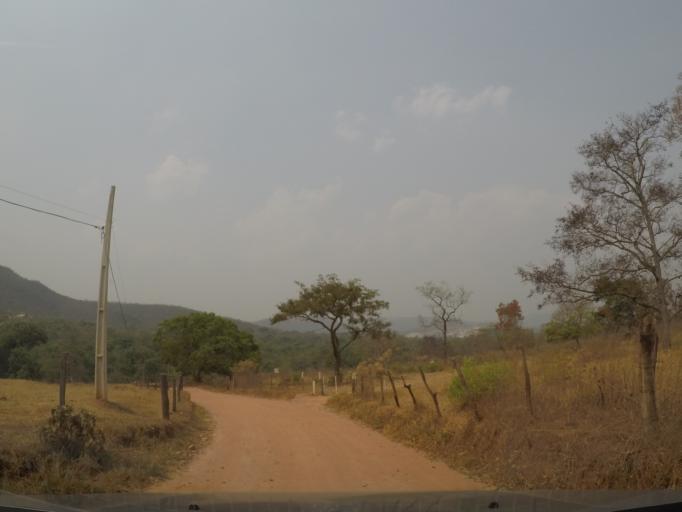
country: BR
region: Goias
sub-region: Pirenopolis
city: Pirenopolis
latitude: -15.8375
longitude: -48.9540
